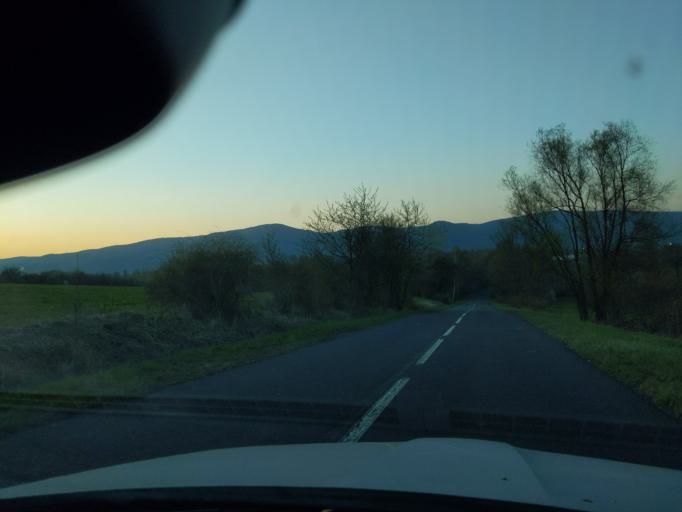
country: CZ
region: Ustecky
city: Chabarovice
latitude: 50.6581
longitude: 13.9140
